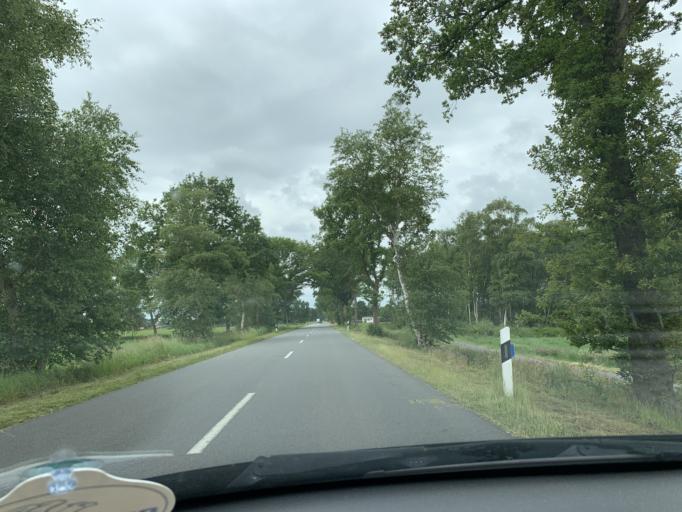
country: DE
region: Lower Saxony
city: Bockhorn
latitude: 53.3229
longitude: 8.0200
